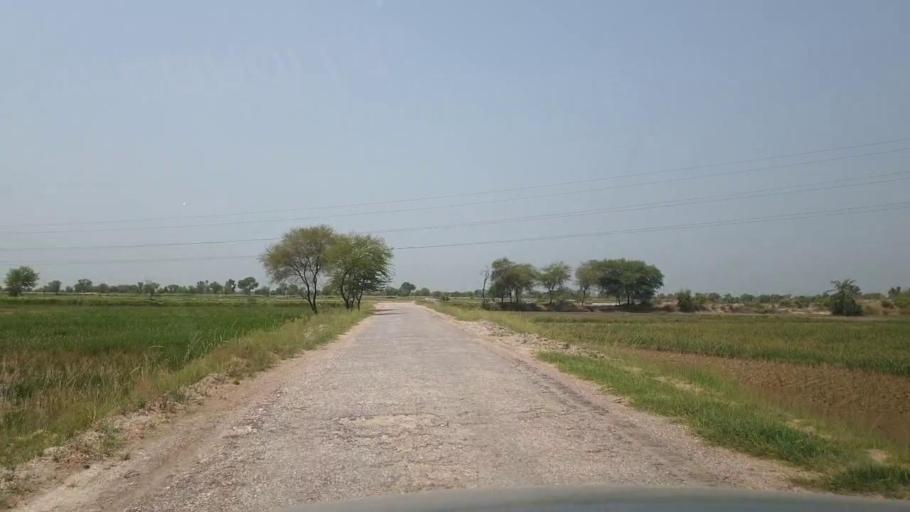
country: PK
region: Sindh
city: Garhi Yasin
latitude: 27.8727
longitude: 68.4478
